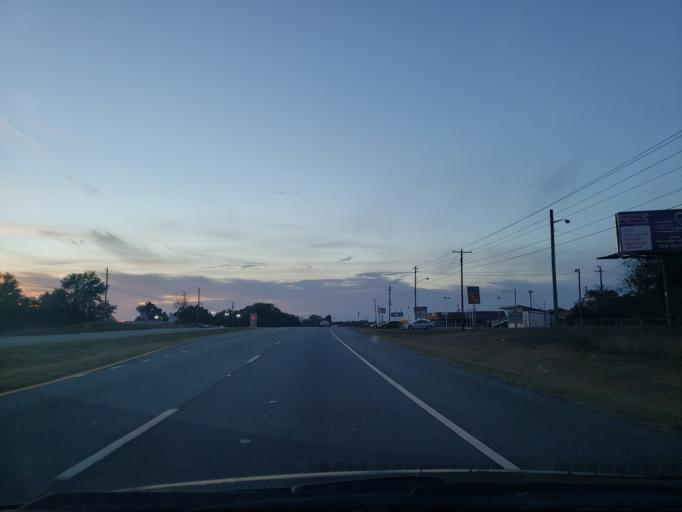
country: US
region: Georgia
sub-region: Dougherty County
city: Albany
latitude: 31.5728
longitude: -84.1253
